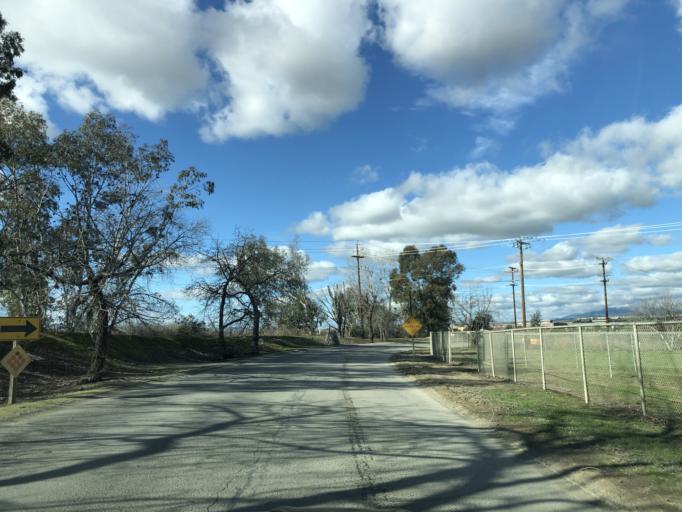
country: US
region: California
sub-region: Alameda County
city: Pleasanton
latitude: 37.6921
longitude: -121.8476
